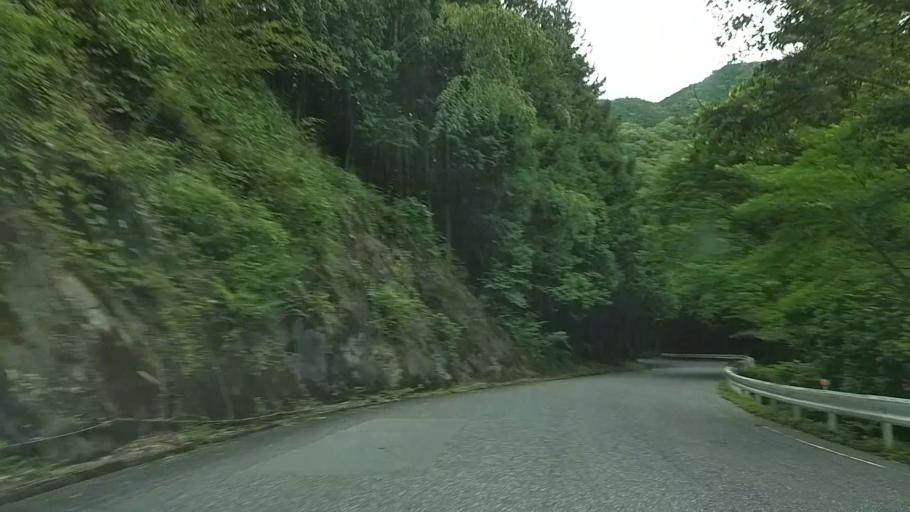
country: JP
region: Yamanashi
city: Otsuki
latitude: 35.5725
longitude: 139.0179
